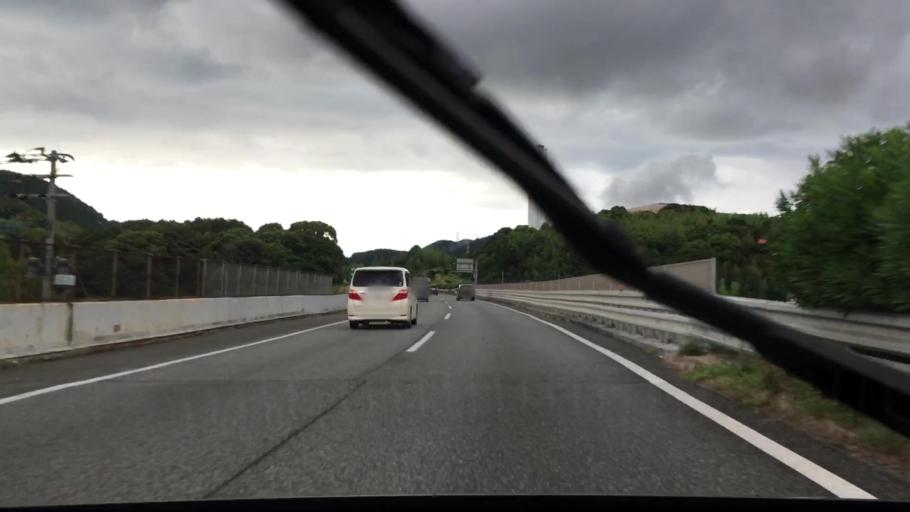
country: JP
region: Fukuoka
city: Sasaguri
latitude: 33.6384
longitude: 130.4896
